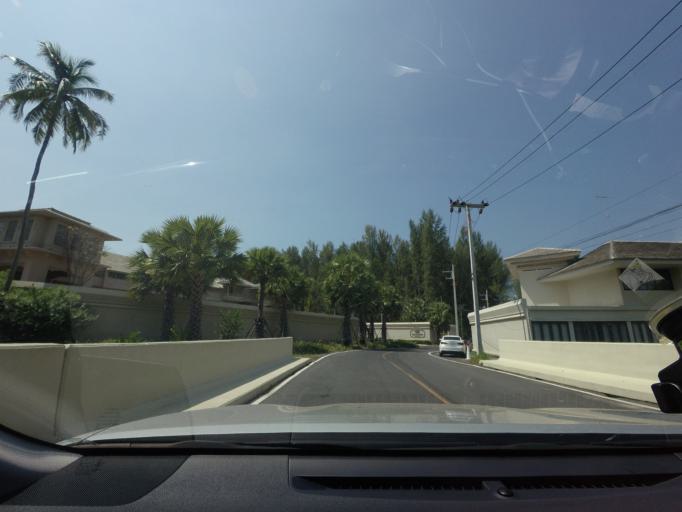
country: TH
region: Phangnga
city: Ban Khao Lak
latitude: 8.6947
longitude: 98.2419
